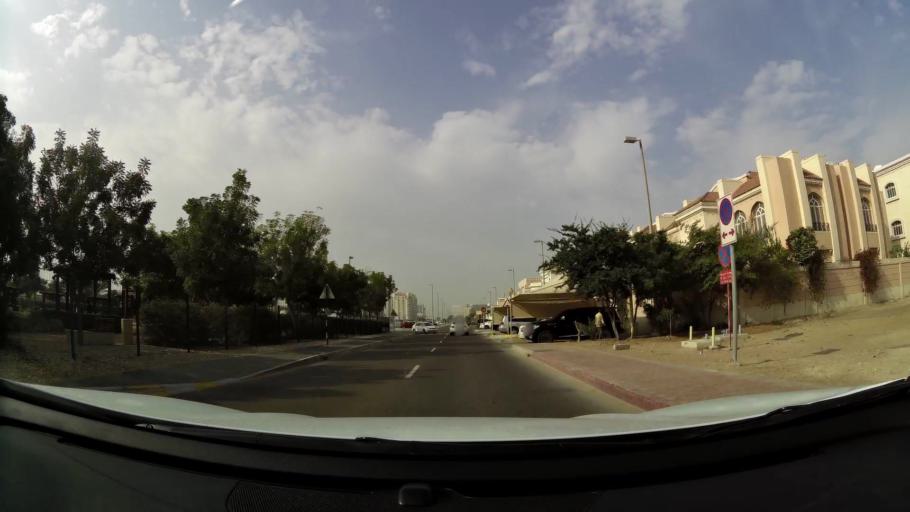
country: AE
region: Abu Dhabi
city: Abu Dhabi
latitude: 24.4732
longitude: 54.3893
